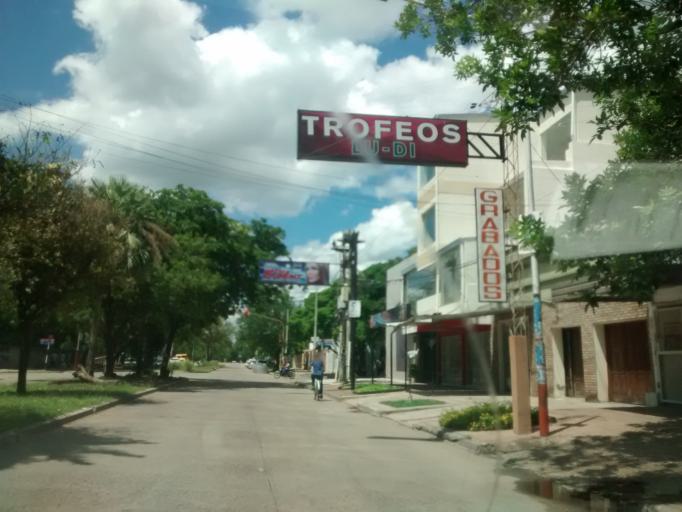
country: AR
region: Chaco
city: Resistencia
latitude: -27.4561
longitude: -58.9921
